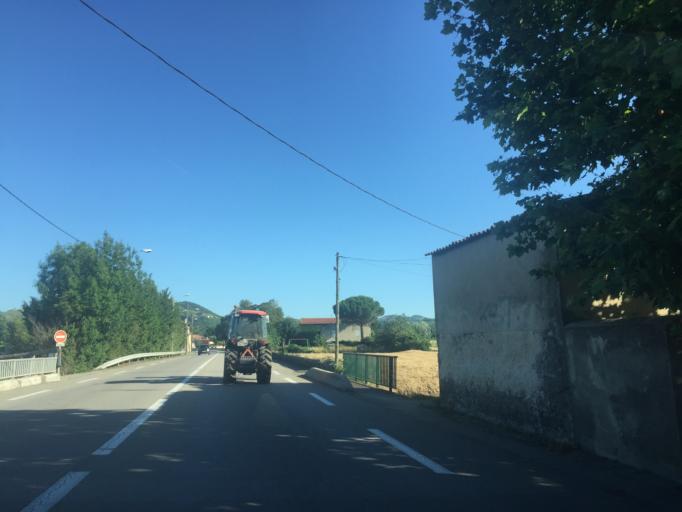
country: FR
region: Rhone-Alpes
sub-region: Departement de l'Ardeche
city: Tournon-sur-Rhone
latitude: 45.0626
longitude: 4.8589
